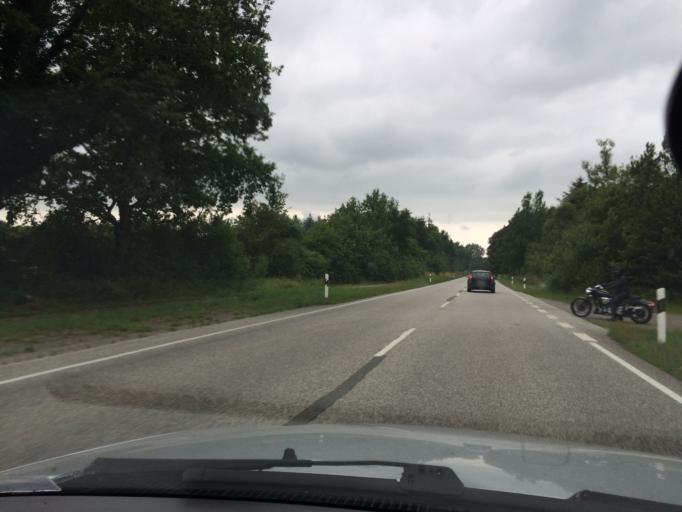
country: DE
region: Schleswig-Holstein
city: Oeversee
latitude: 54.6878
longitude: 9.4326
